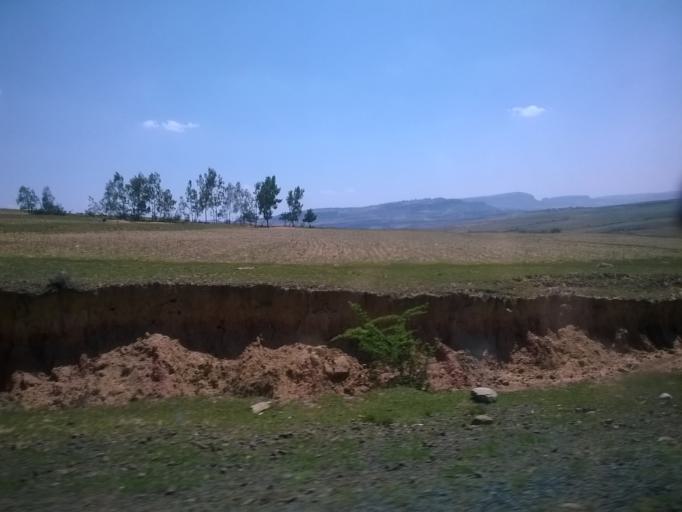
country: LS
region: Berea
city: Teyateyaneng
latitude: -29.1031
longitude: 27.8400
